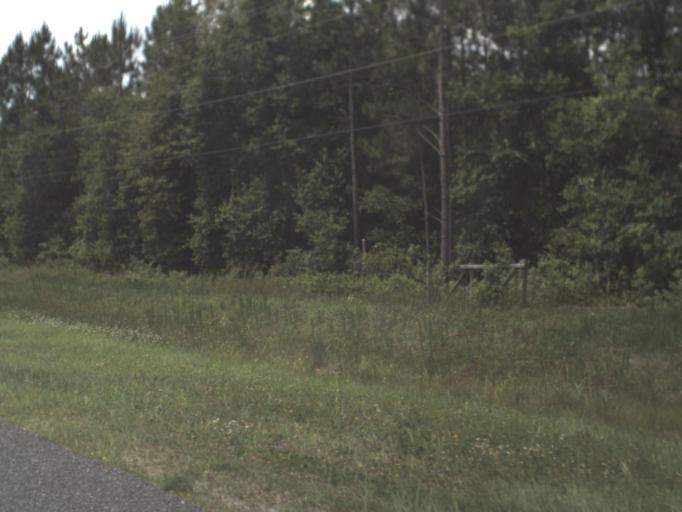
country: US
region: Florida
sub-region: Putnam County
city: East Palatka
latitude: 29.7975
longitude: -81.6526
